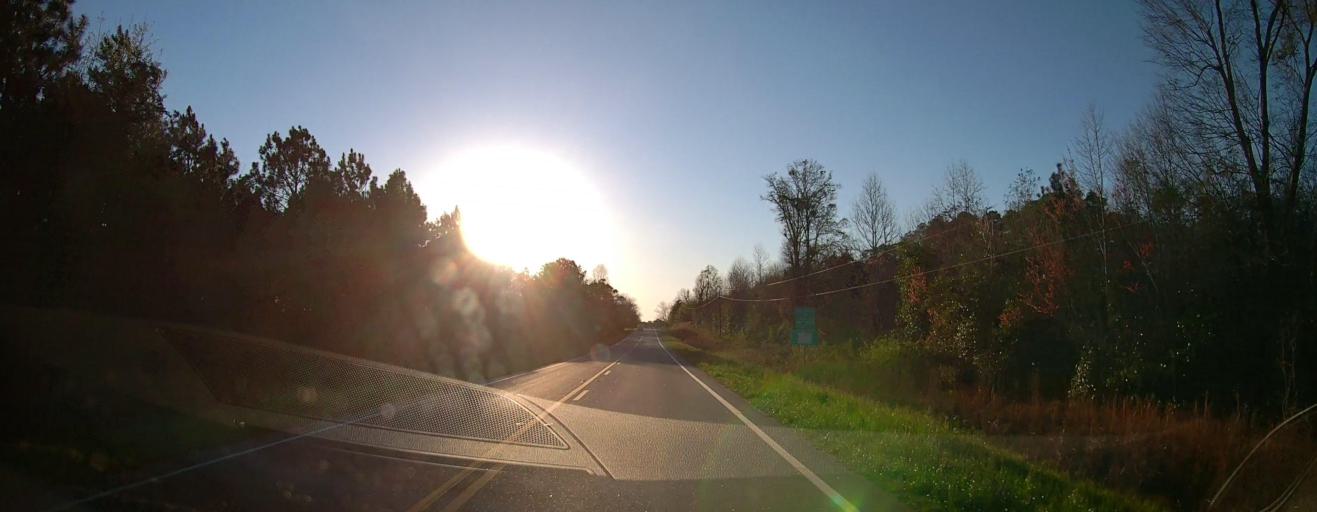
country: US
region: Georgia
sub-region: Wilcox County
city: Rochelle
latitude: 31.9452
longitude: -83.5176
